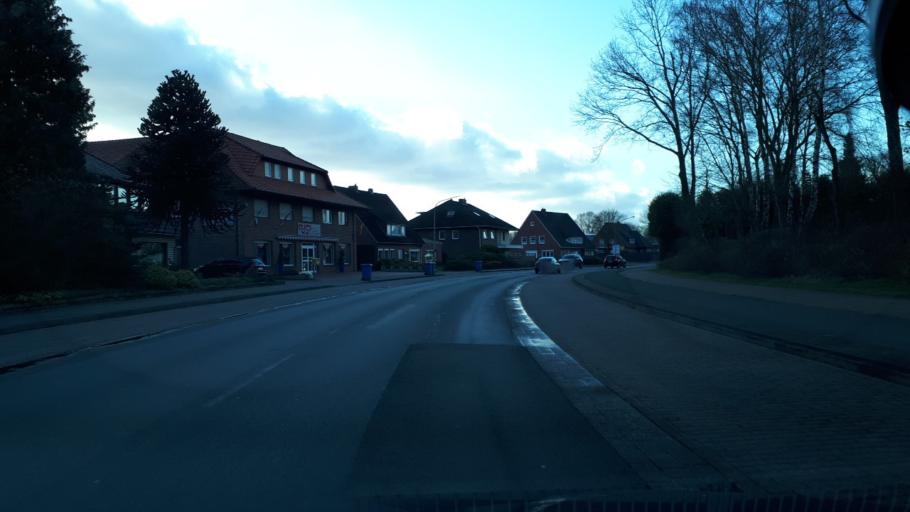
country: DE
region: Lower Saxony
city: Molbergen
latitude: 52.8591
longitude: 7.9164
